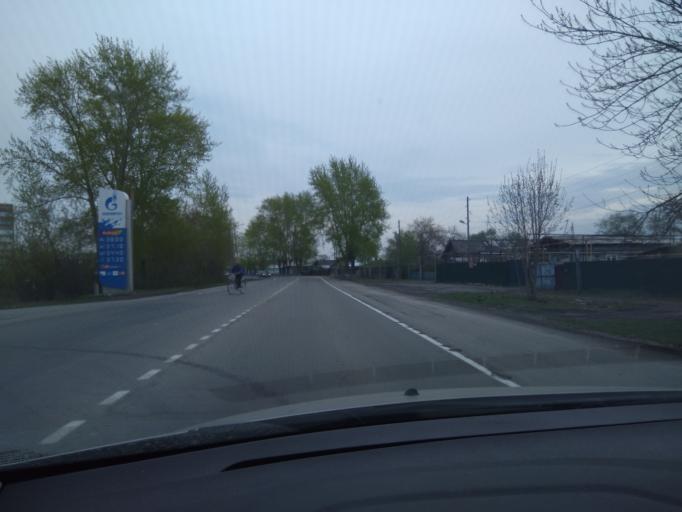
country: RU
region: Sverdlovsk
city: Bogdanovich
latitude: 56.7742
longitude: 62.0354
